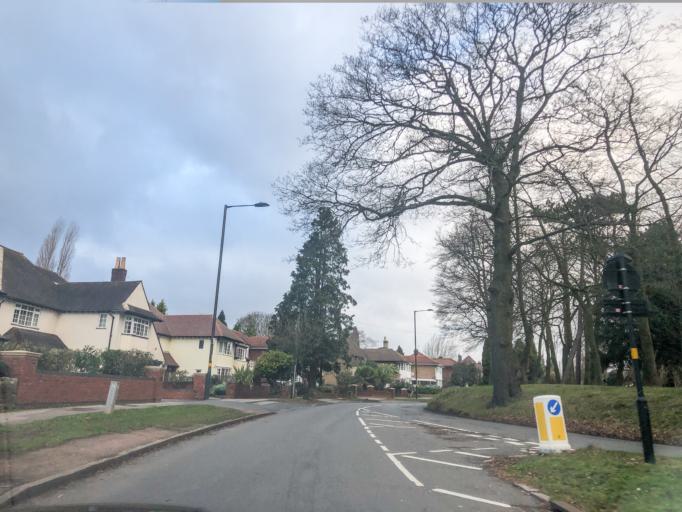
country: GB
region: England
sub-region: City and Borough of Birmingham
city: Birmingham
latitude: 52.4410
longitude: -1.9052
